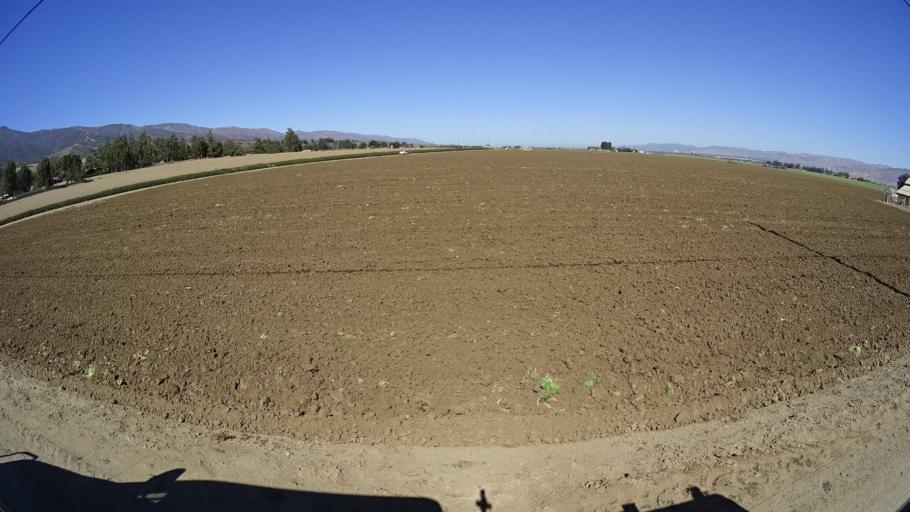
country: US
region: California
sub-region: Monterey County
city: Soledad
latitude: 36.3913
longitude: -121.3585
